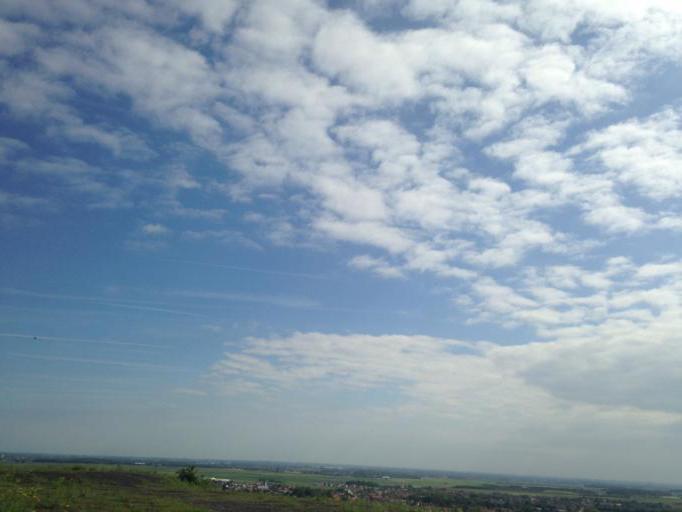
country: FR
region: Nord-Pas-de-Calais
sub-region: Departement du Pas-de-Calais
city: Loos-en-Gohelle
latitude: 50.4473
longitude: 2.7811
